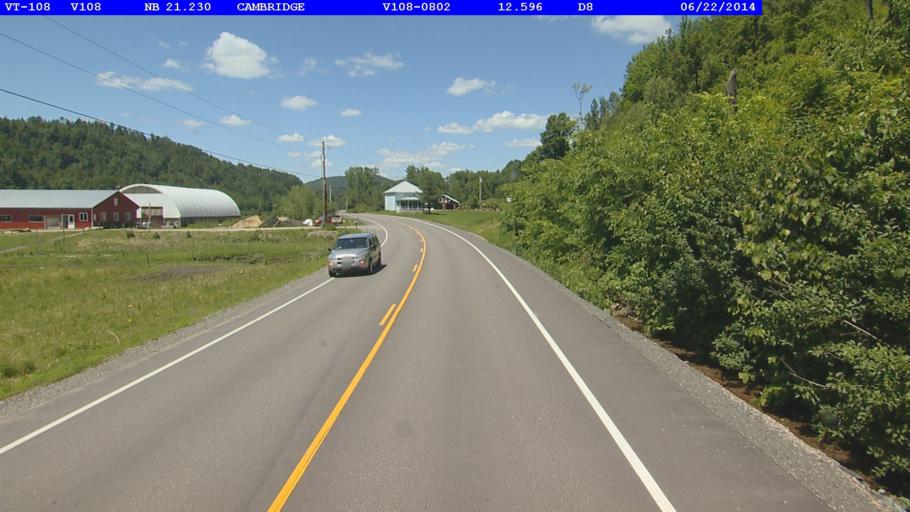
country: US
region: Vermont
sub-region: Lamoille County
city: Johnson
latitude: 44.6967
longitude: -72.8279
